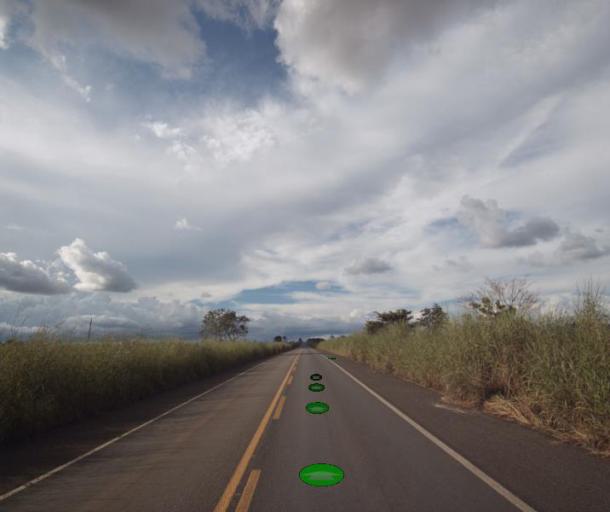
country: BR
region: Goias
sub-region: Niquelandia
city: Niquelandia
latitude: -14.7616
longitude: -48.6226
